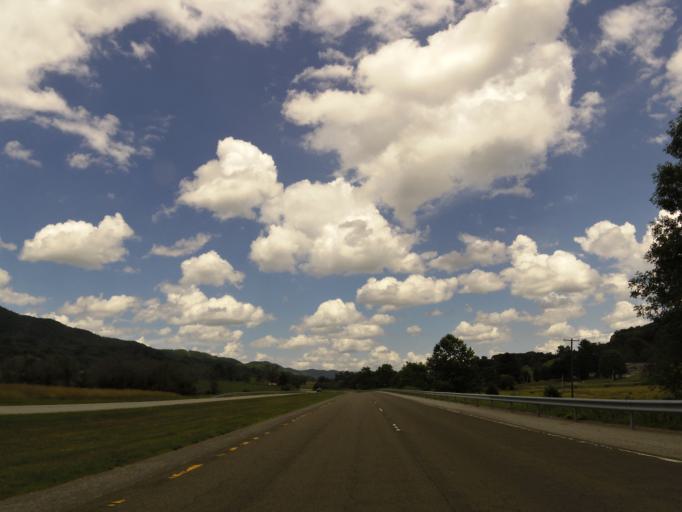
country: US
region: Kentucky
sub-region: Harlan County
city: Loyall
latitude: 36.6541
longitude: -83.4022
